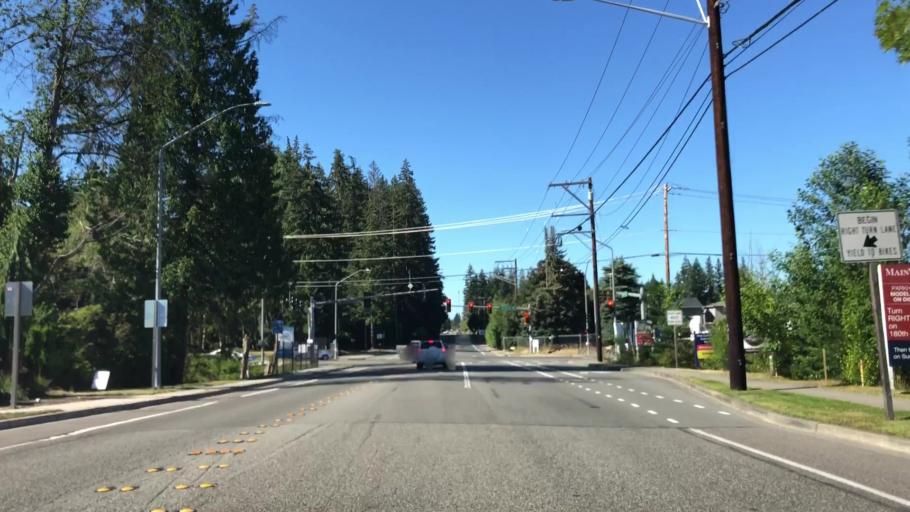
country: US
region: Washington
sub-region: Snohomish County
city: North Creek
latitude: 47.8338
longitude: -122.1858
